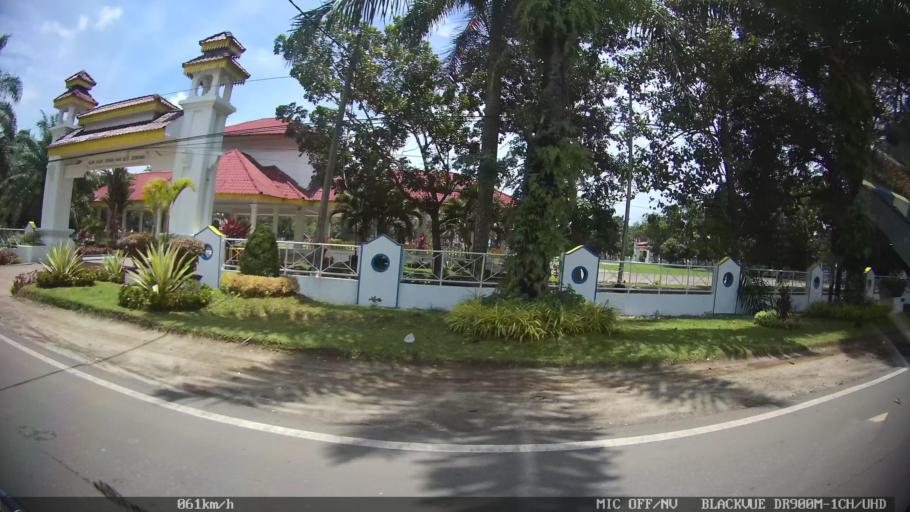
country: ID
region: North Sumatra
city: Percut
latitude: 3.5497
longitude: 98.8656
